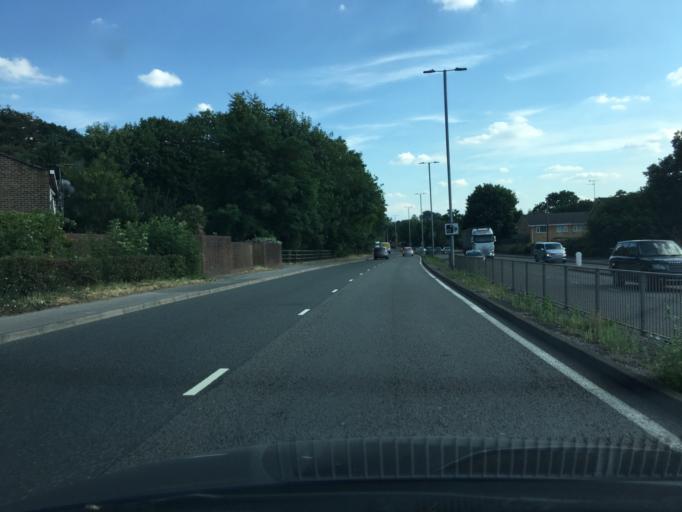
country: GB
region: England
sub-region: Bracknell Forest
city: Bracknell
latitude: 51.4052
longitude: -0.7473
